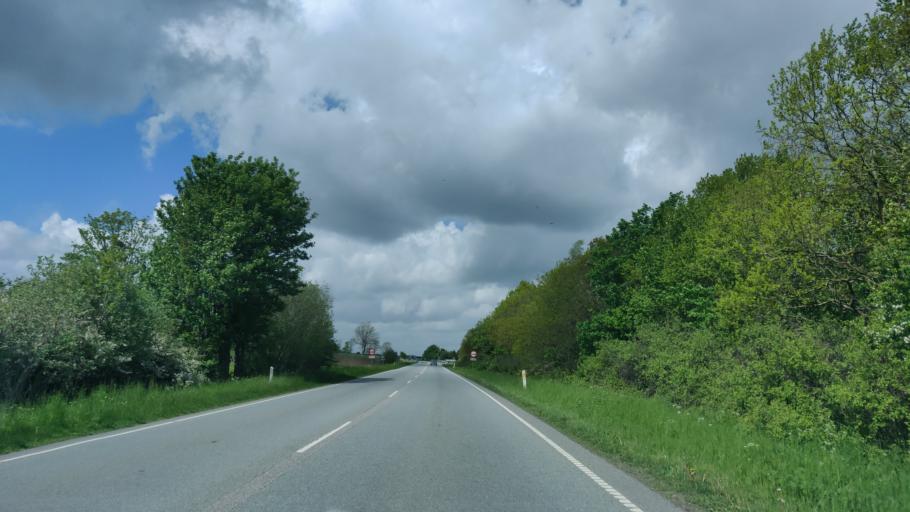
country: DK
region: Central Jutland
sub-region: Hedensted Kommune
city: Torring
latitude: 55.8408
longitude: 9.5032
